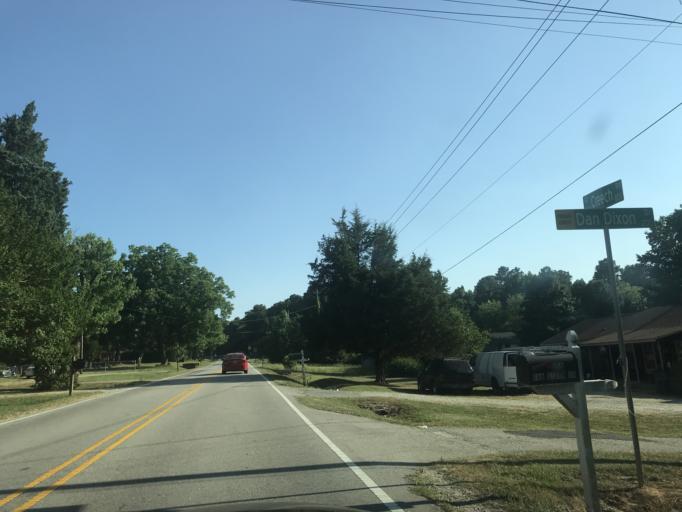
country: US
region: North Carolina
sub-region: Wake County
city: Garner
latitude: 35.7202
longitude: -78.6016
